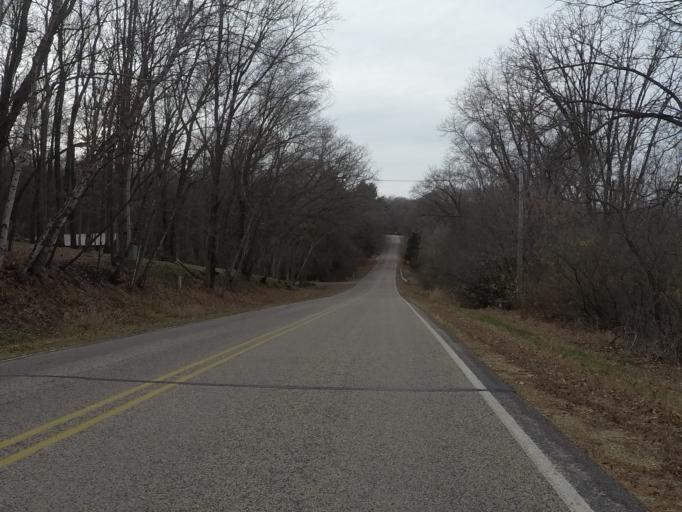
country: US
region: Wisconsin
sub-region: Dane County
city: Middleton
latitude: 43.0820
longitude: -89.5709
